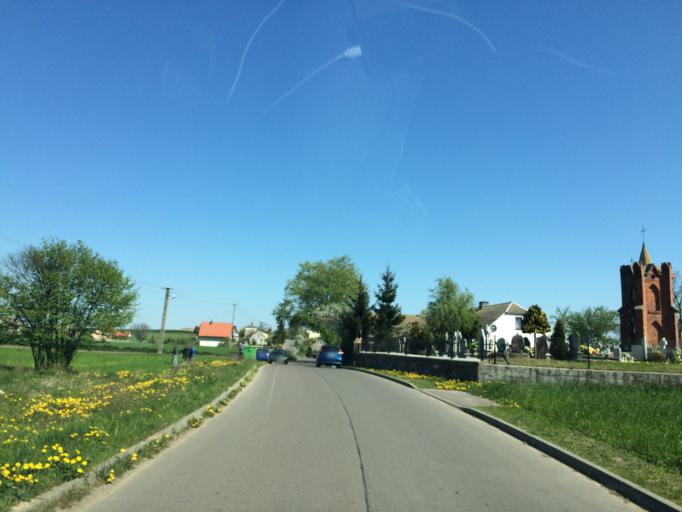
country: PL
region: Warmian-Masurian Voivodeship
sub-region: Powiat nowomiejski
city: Biskupiec
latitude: 53.5383
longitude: 19.4609
